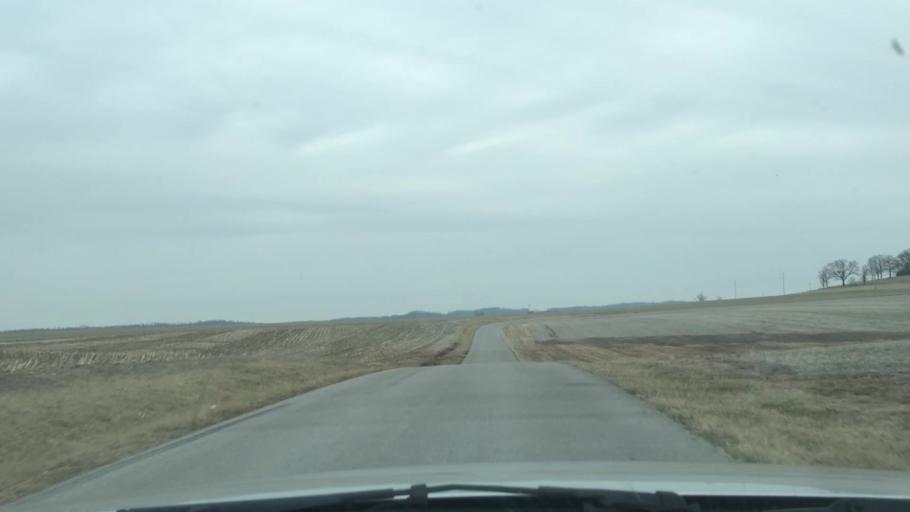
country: US
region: Kentucky
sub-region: Edmonson County
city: Brownsville
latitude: 37.0524
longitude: -86.2405
